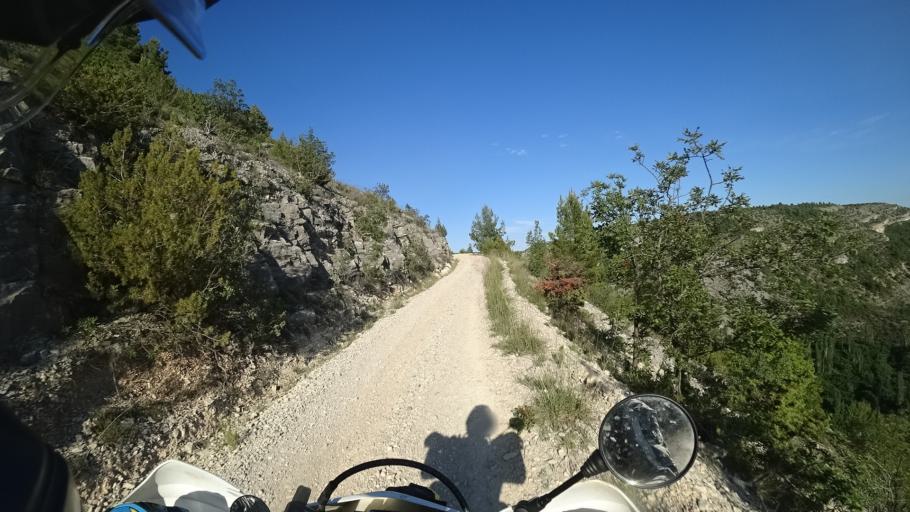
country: HR
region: Sibensko-Kniniska
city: Drnis
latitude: 43.8295
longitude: 16.0242
